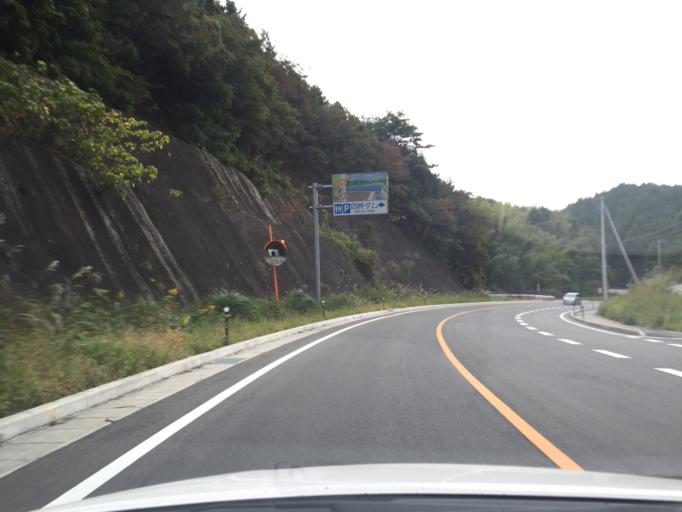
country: JP
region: Ibaraki
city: Kitaibaraki
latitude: 36.9084
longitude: 140.7214
